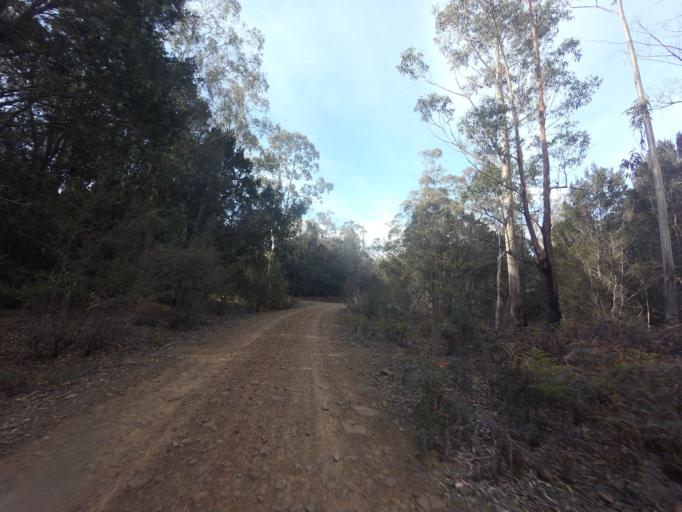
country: AU
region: Tasmania
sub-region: Break O'Day
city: St Helens
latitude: -41.8410
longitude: 148.0864
